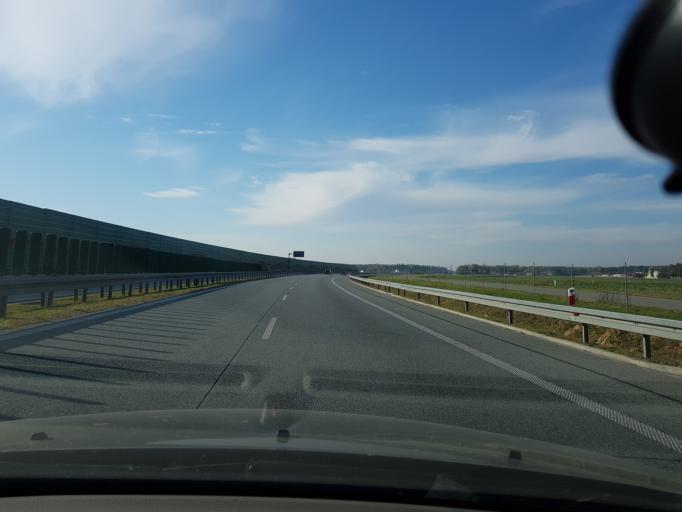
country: PL
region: Lodz Voivodeship
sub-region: Powiat tomaszowski
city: Czerniewice
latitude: 51.6502
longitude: 20.1447
